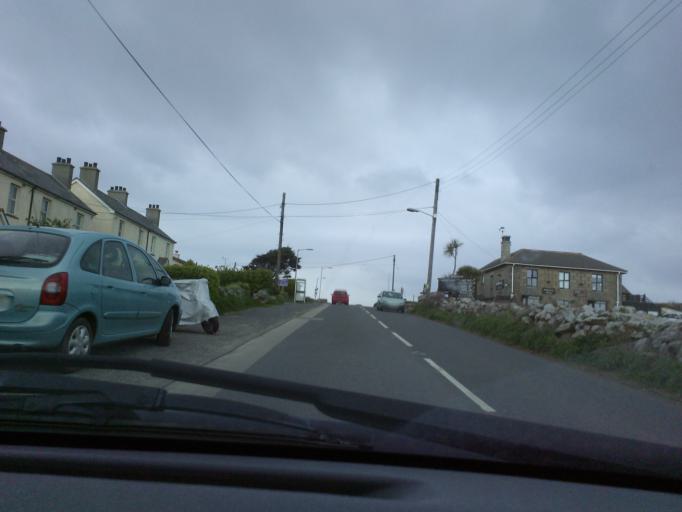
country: GB
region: England
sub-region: Cornwall
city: Sennen
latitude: 50.0790
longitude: -5.6833
